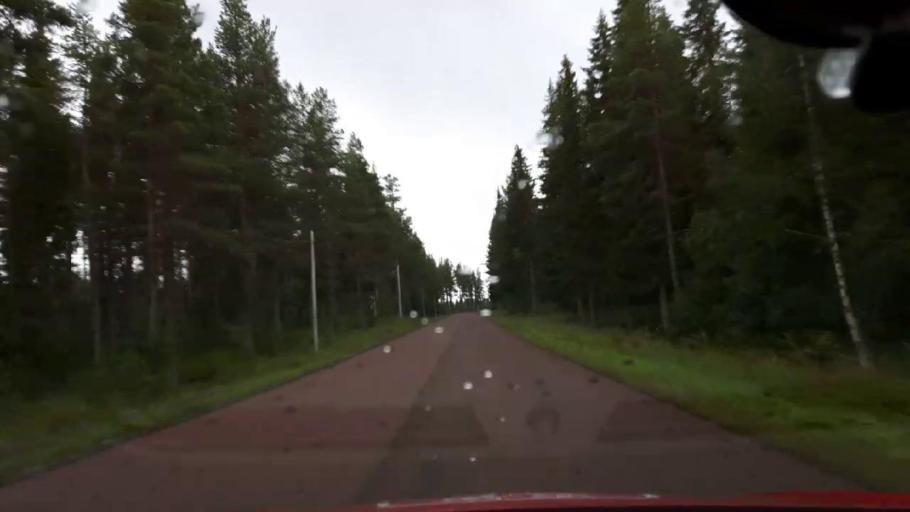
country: SE
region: Jaemtland
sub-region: Are Kommun
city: Jarpen
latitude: 63.3197
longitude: 13.6947
